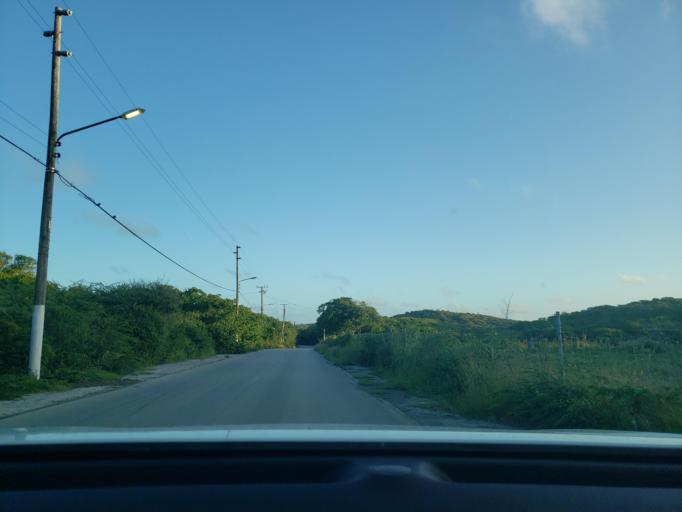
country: CW
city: Barber
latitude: 12.2649
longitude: -69.0669
